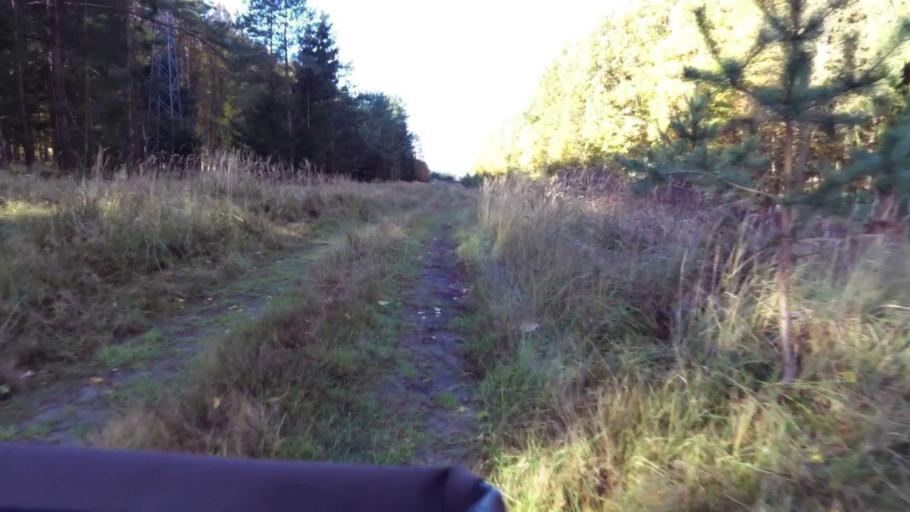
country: PL
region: West Pomeranian Voivodeship
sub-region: Powiat kamienski
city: Miedzyzdroje
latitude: 53.8695
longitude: 14.4972
